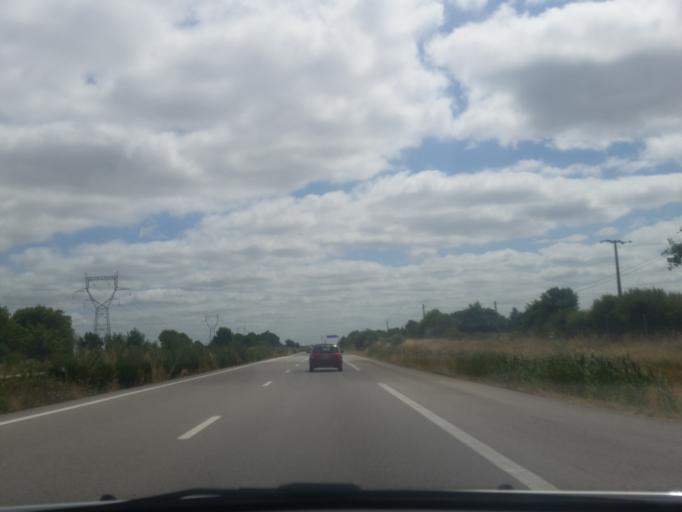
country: FR
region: Pays de la Loire
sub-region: Departement de la Loire-Atlantique
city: Varades
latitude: 47.4205
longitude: -1.0266
